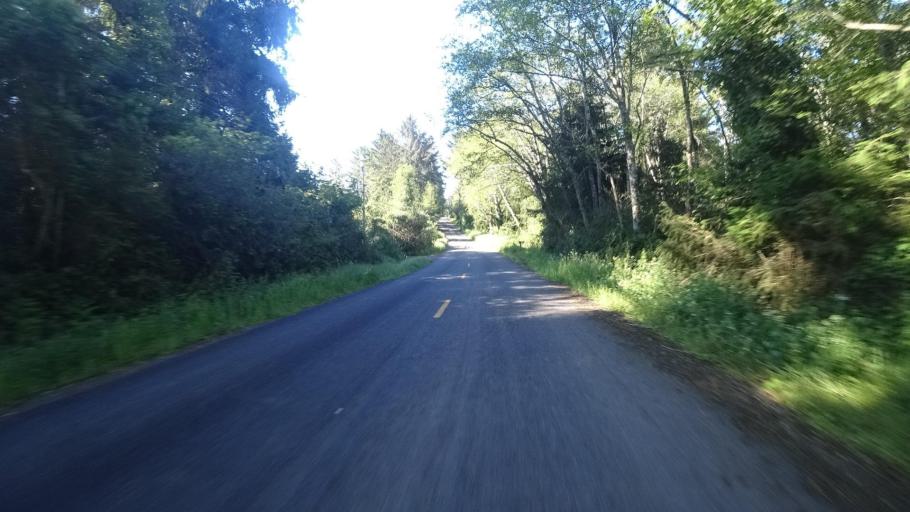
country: US
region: California
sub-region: Humboldt County
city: Westhaven-Moonstone
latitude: 40.9997
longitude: -124.1006
